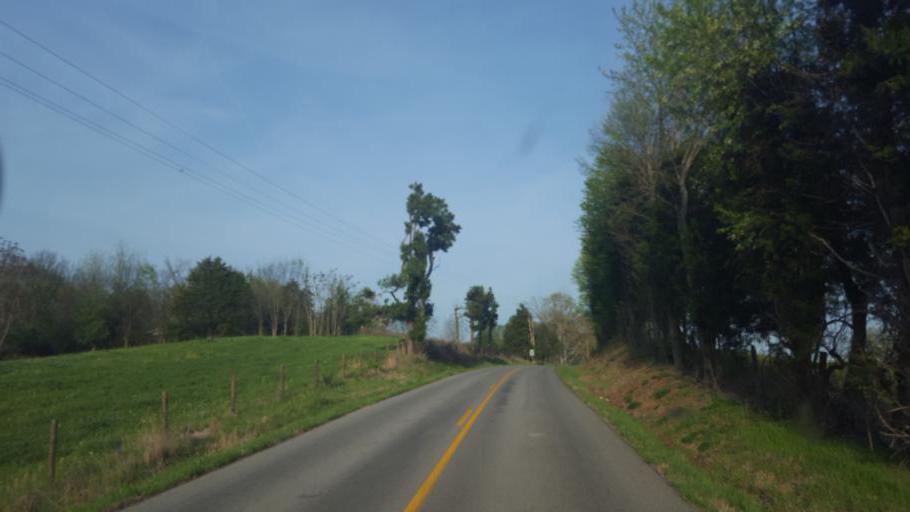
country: US
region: Kentucky
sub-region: Barren County
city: Glasgow
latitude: 36.9483
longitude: -86.0069
